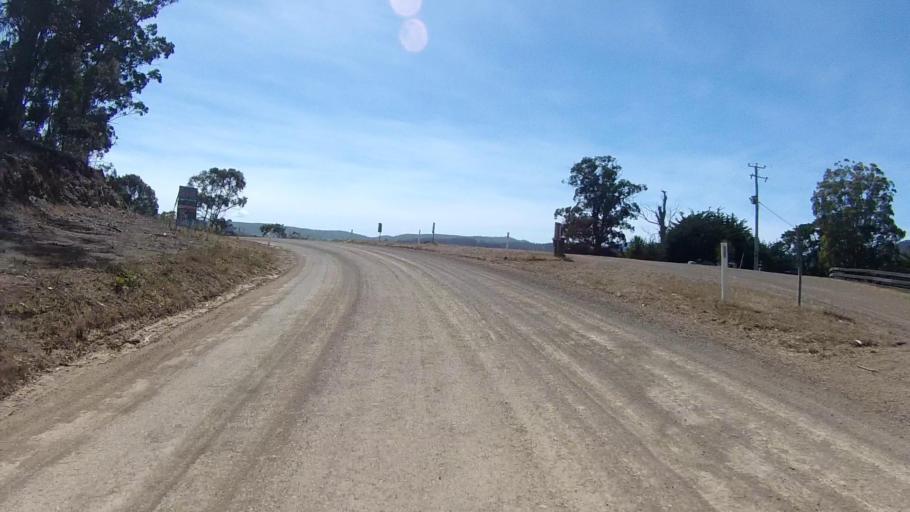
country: AU
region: Tasmania
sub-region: Sorell
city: Sorell
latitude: -42.7583
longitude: 147.6805
